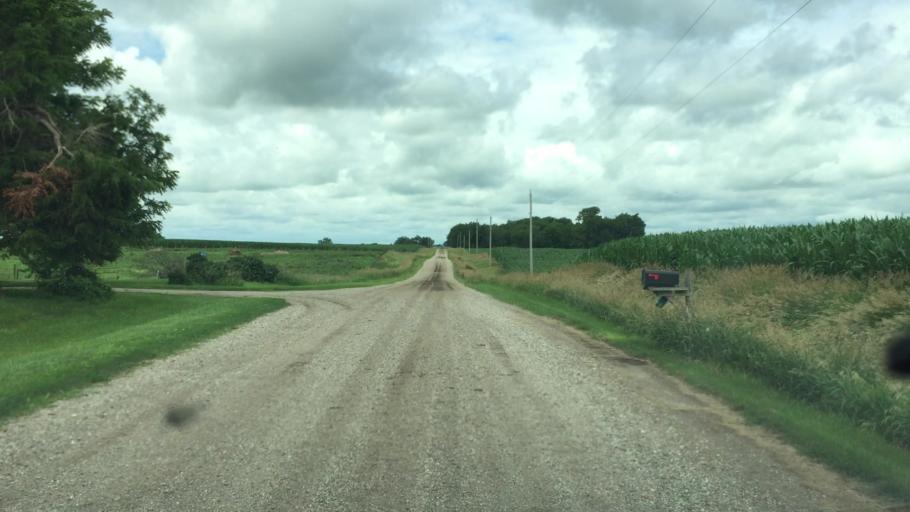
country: US
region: Iowa
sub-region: Jasper County
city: Monroe
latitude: 41.5662
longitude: -93.1088
